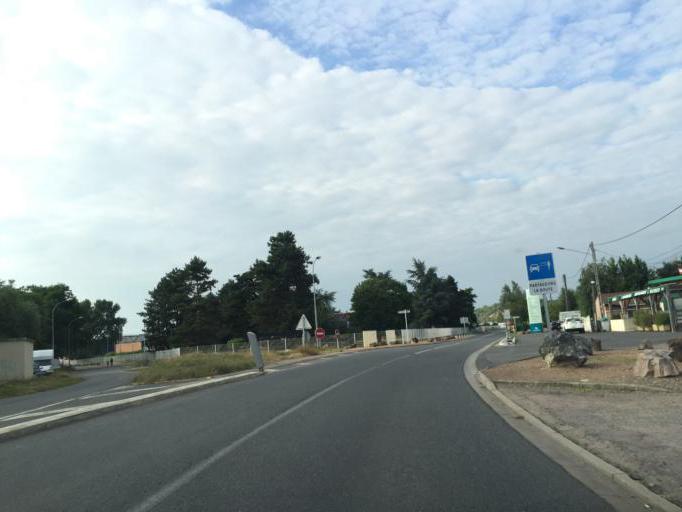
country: FR
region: Auvergne
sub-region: Departement de l'Allier
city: Creuzier-le-Vieux
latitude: 46.1553
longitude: 3.4106
